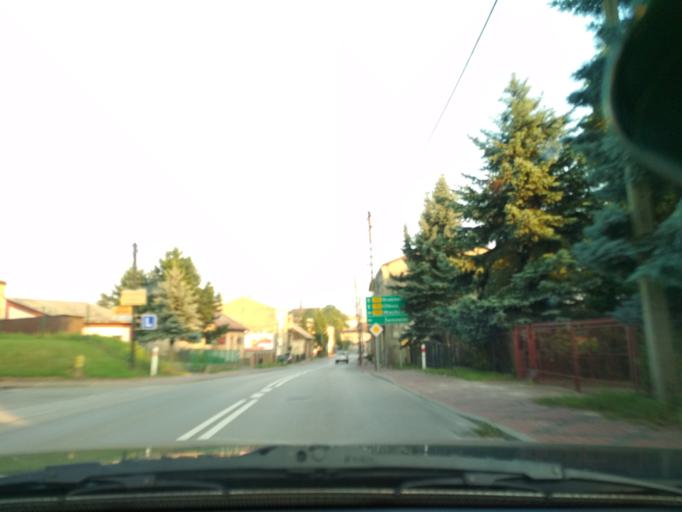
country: PL
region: Lesser Poland Voivodeship
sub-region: Powiat olkuski
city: Wolbrom
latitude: 50.3897
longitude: 19.7568
